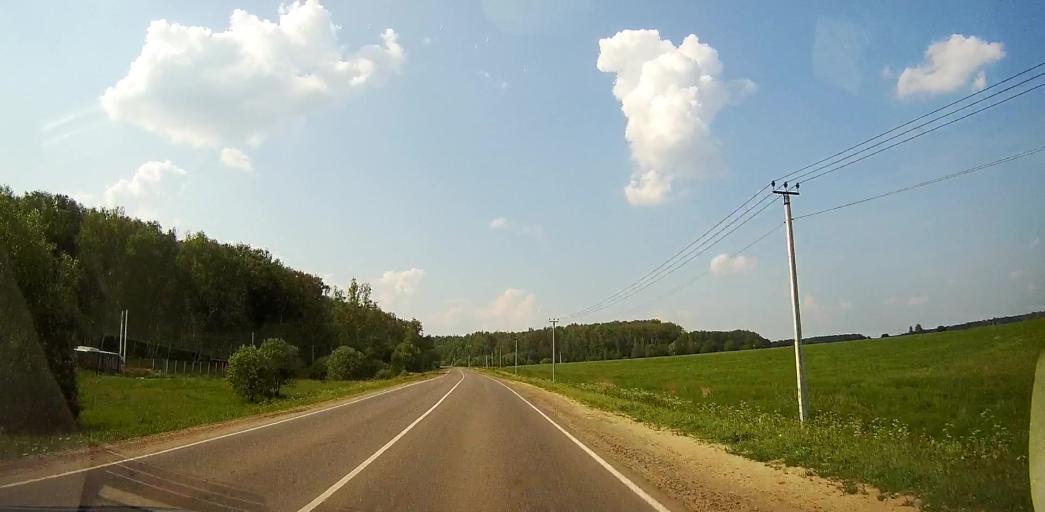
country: RU
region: Moskovskaya
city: Il'inskoye
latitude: 55.2074
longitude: 37.9607
